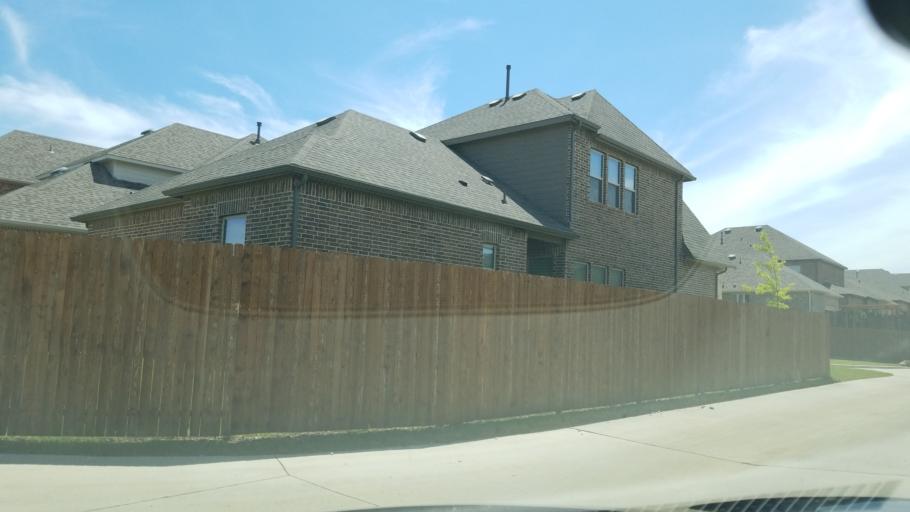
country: US
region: Texas
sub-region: Dallas County
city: Coppell
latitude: 32.8797
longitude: -96.9949
